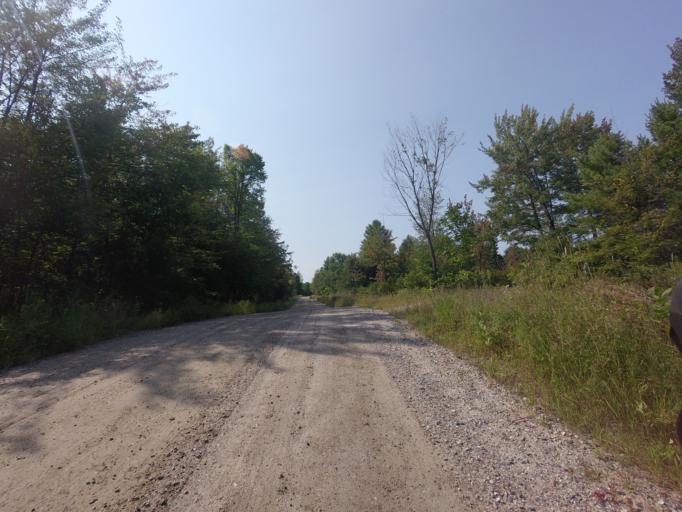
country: CA
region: Ontario
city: Skatepark
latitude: 44.7100
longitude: -76.7614
